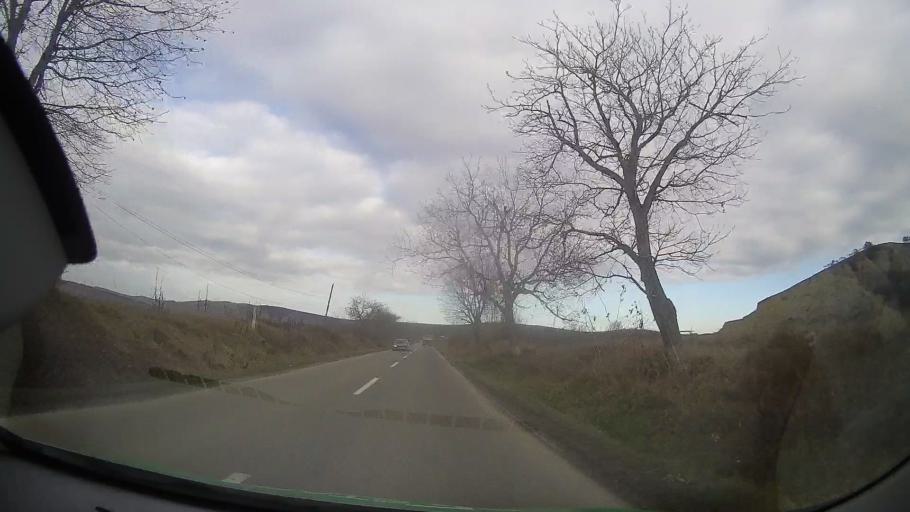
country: RO
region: Mures
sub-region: Comuna Iernut
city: Iernut
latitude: 46.4649
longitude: 24.2183
